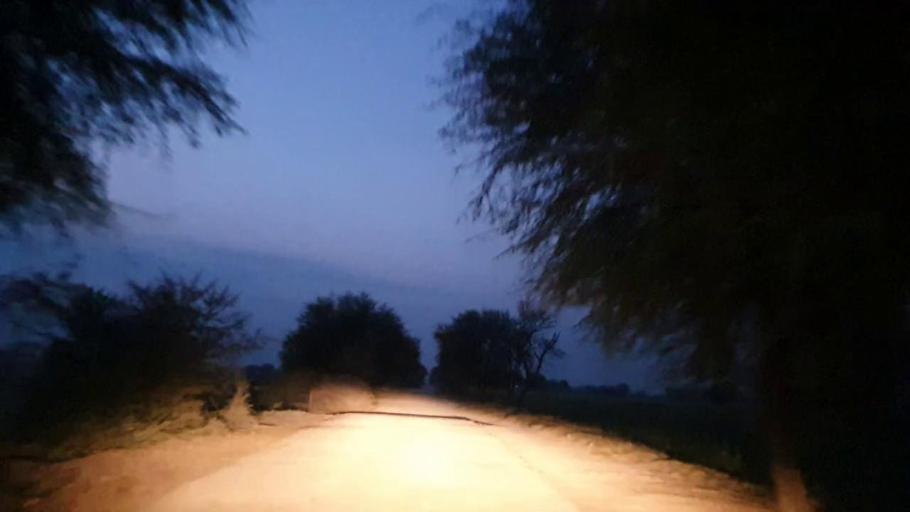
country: PK
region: Sindh
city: Tando Ghulam Ali
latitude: 25.0822
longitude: 68.9224
